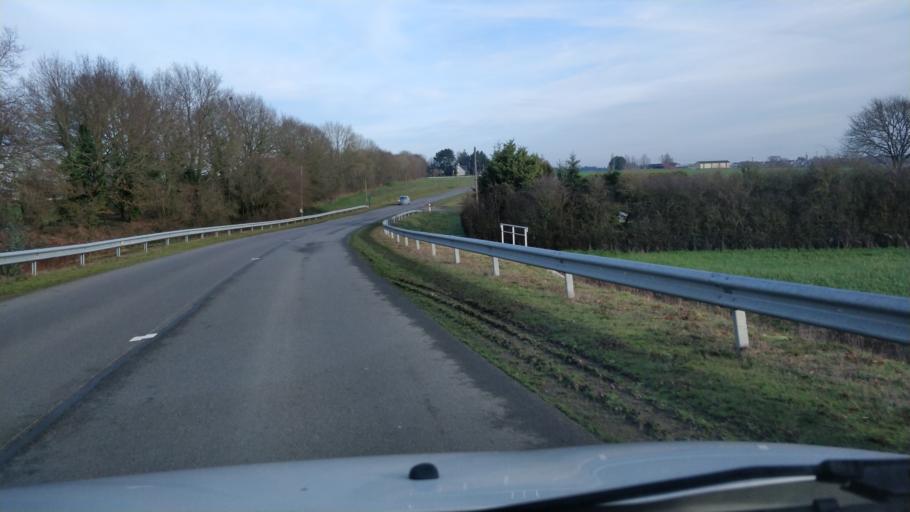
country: FR
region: Brittany
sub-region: Departement d'Ille-et-Vilaine
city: Argentre-du-Plessis
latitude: 48.0450
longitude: -1.1670
